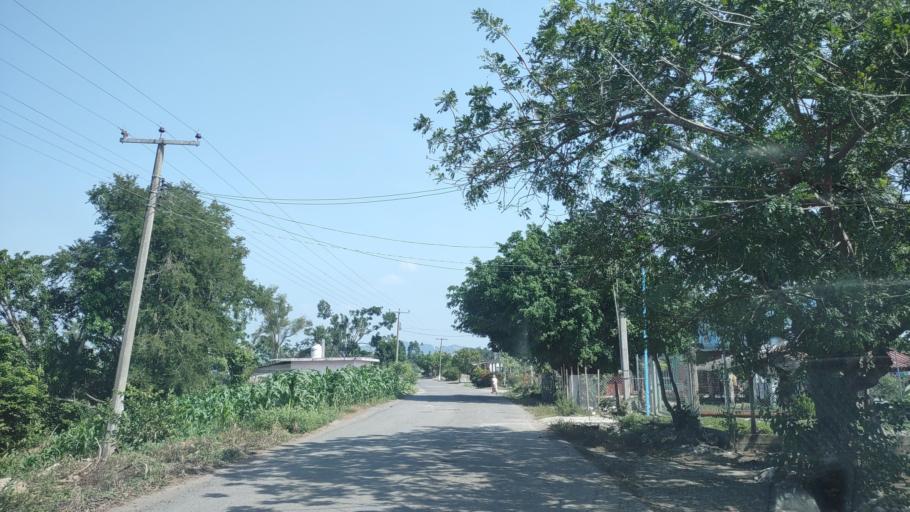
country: MX
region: Puebla
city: Espinal
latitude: 20.2572
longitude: -97.3228
